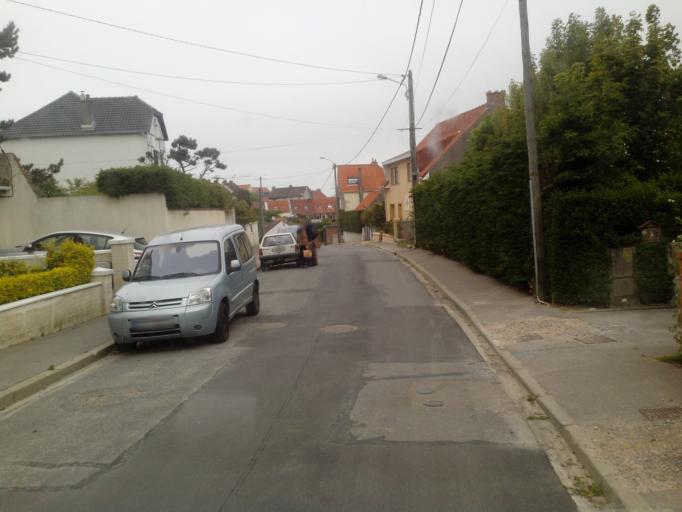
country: FR
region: Nord-Pas-de-Calais
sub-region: Departement du Pas-de-Calais
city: Wimereux
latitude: 50.7628
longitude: 1.6164
